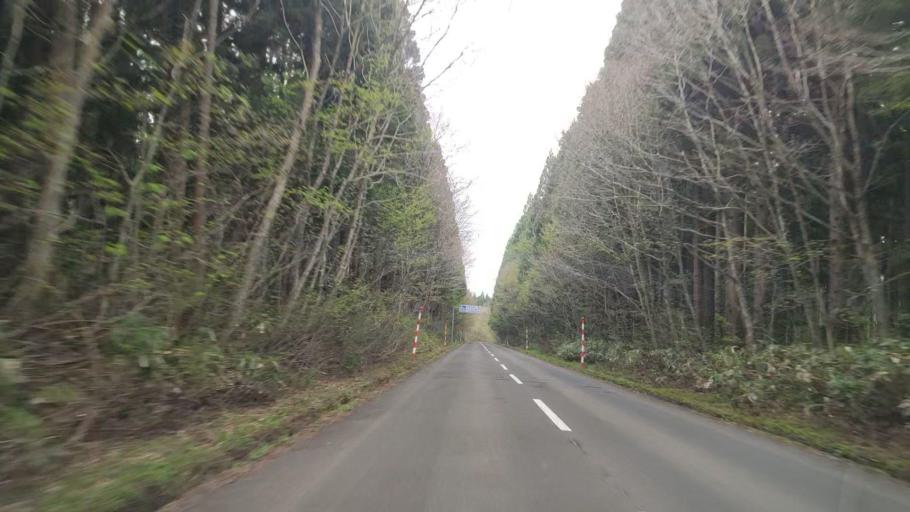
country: JP
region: Akita
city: Hanawa
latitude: 40.3868
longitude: 140.7930
